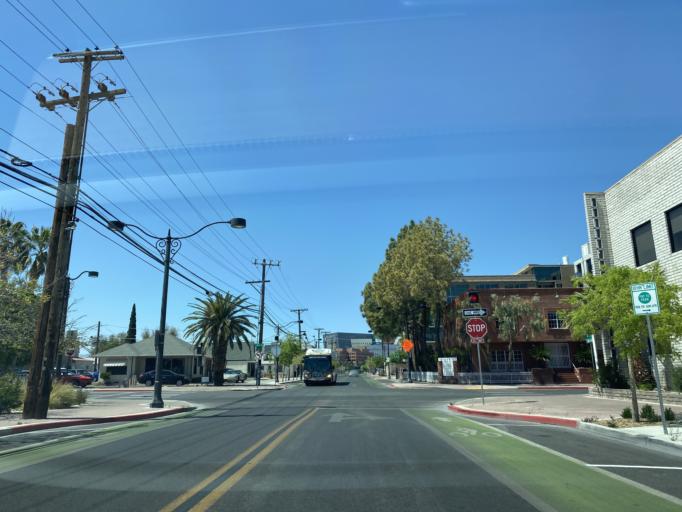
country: US
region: Nevada
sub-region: Clark County
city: Las Vegas
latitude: 36.1626
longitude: -115.1460
